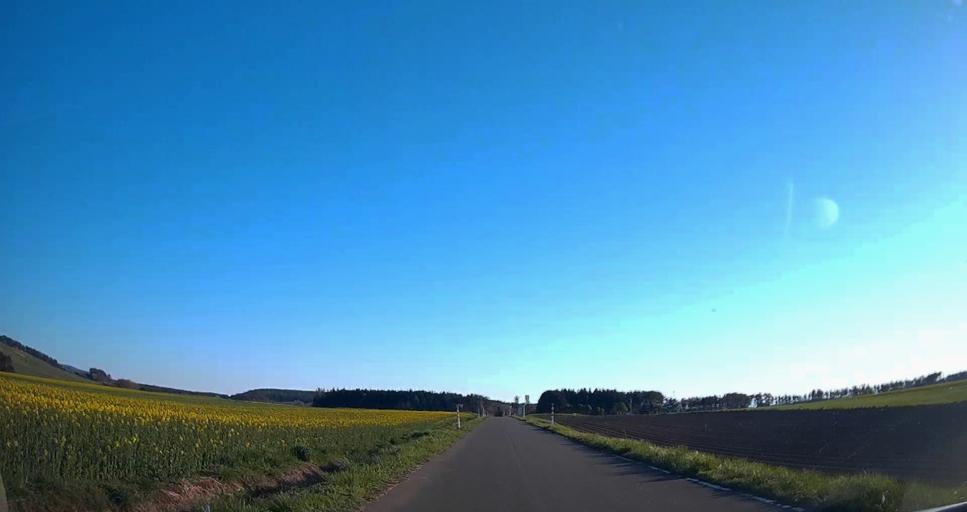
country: JP
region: Aomori
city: Mutsu
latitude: 41.1158
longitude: 141.2741
